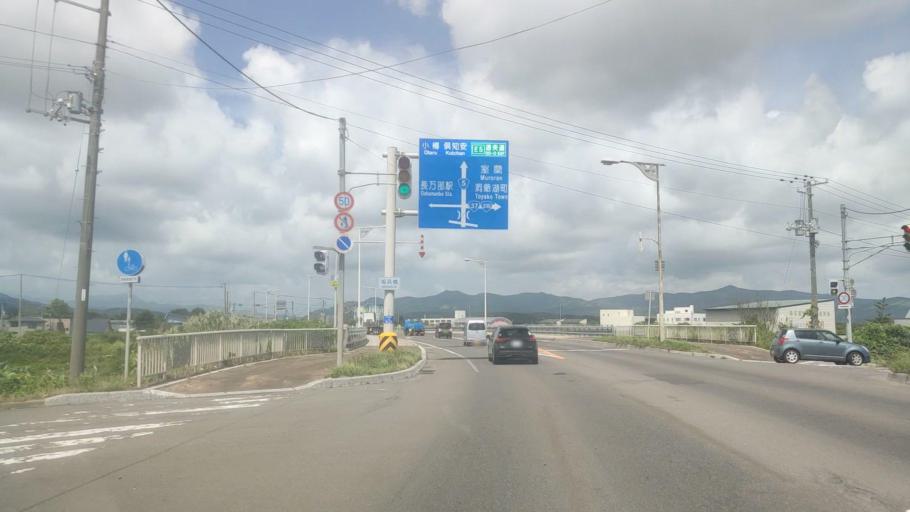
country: JP
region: Hokkaido
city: Niseko Town
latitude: 42.5165
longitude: 140.3824
